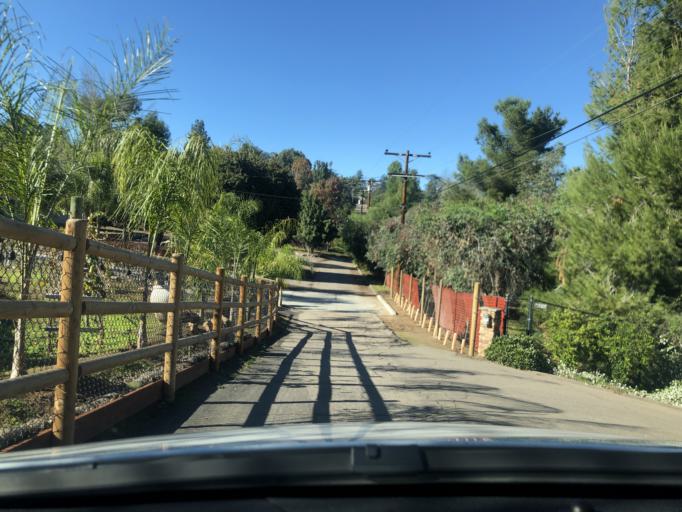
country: US
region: California
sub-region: San Diego County
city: Rancho San Diego
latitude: 32.7715
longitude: -116.9440
